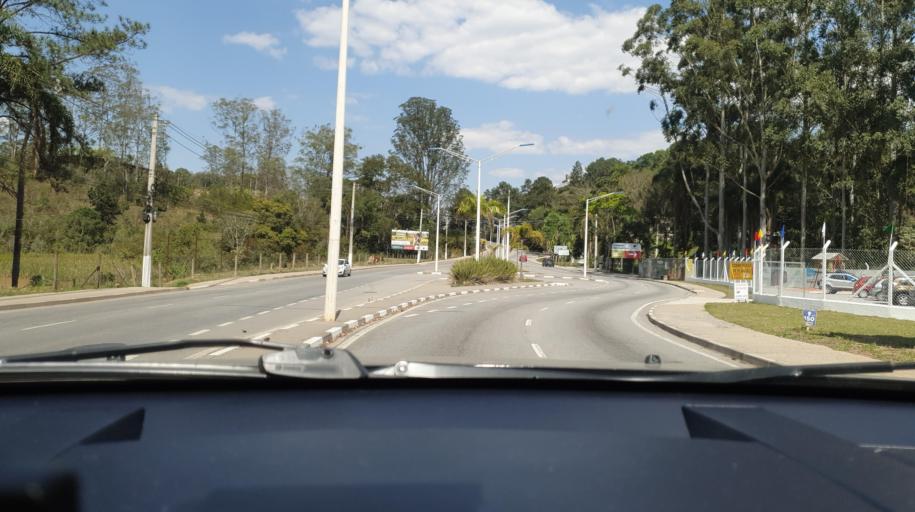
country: BR
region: Sao Paulo
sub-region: Vargem Grande Paulista
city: Vargem Grande Paulista
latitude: -23.6322
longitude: -46.9875
